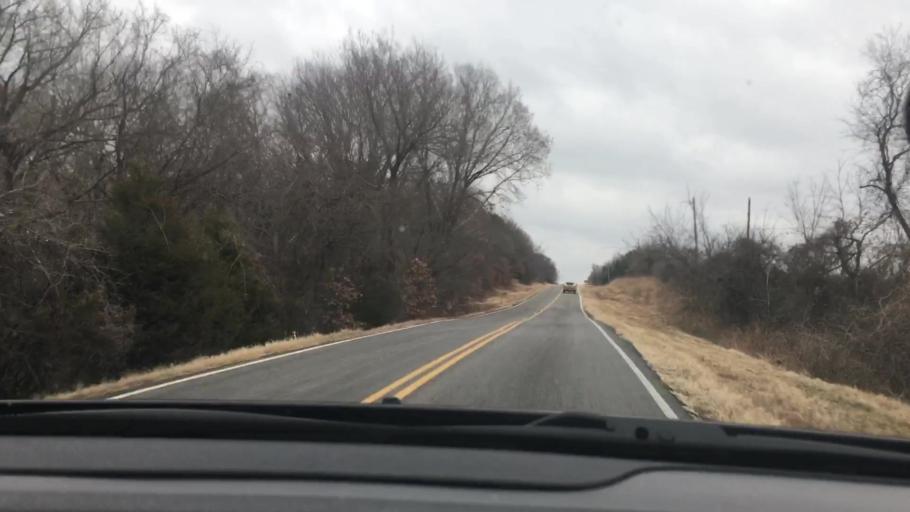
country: US
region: Oklahoma
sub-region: Johnston County
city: Tishomingo
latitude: 34.2087
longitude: -96.6153
